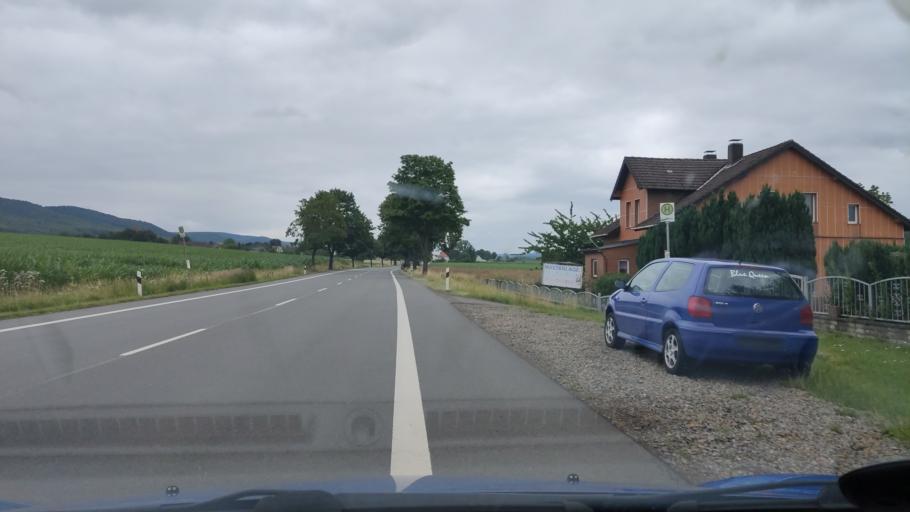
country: DE
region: Lower Saxony
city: Luerdissen
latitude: 51.9538
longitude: 9.6127
